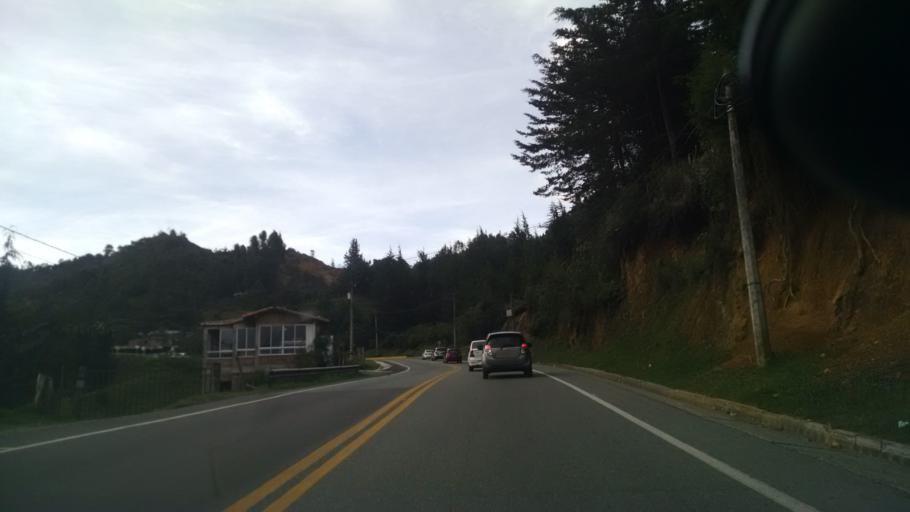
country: CO
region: Antioquia
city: El Retiro
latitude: 6.1356
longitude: -75.5098
